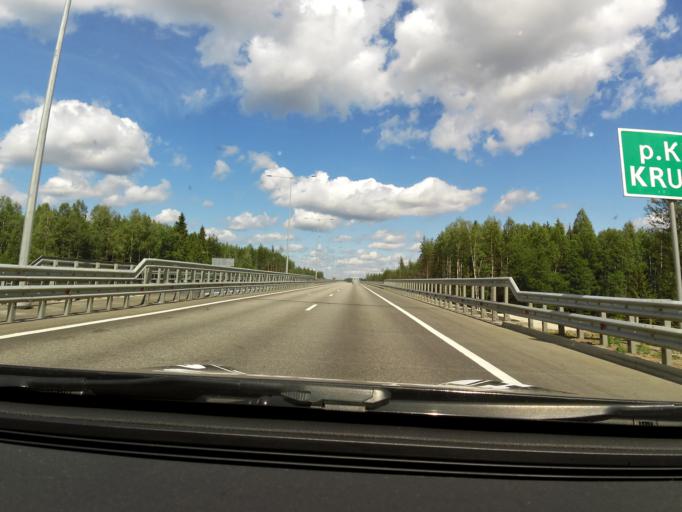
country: RU
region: Tverskaya
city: Krasnomayskiy
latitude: 57.6001
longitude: 34.2510
